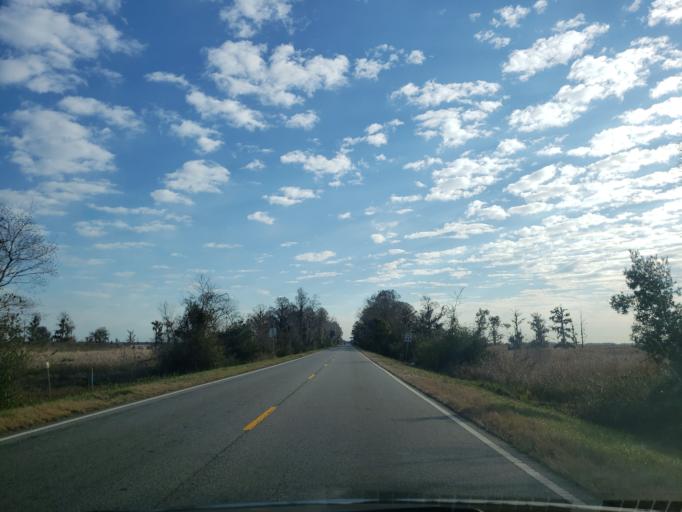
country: US
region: Georgia
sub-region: Chatham County
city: Port Wentworth
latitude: 32.1656
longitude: -81.1454
